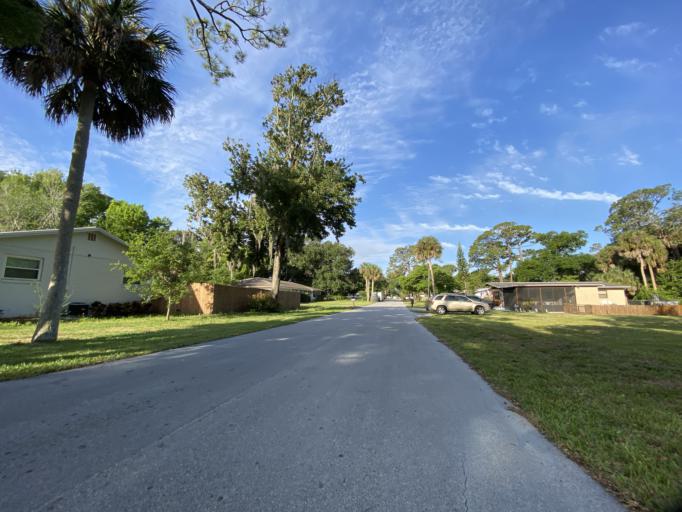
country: US
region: Florida
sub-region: Volusia County
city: South Daytona
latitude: 29.1735
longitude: -81.0083
